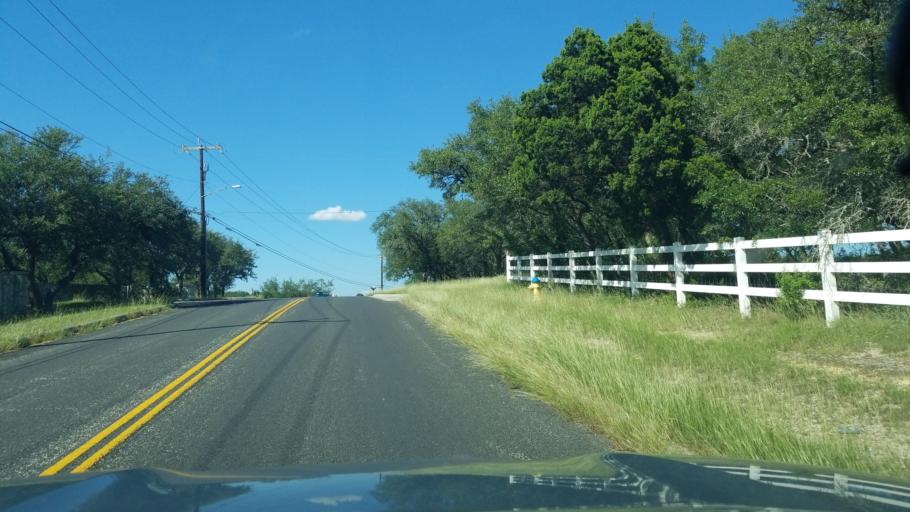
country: US
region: Texas
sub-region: Bexar County
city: Timberwood Park
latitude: 29.6780
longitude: -98.4970
